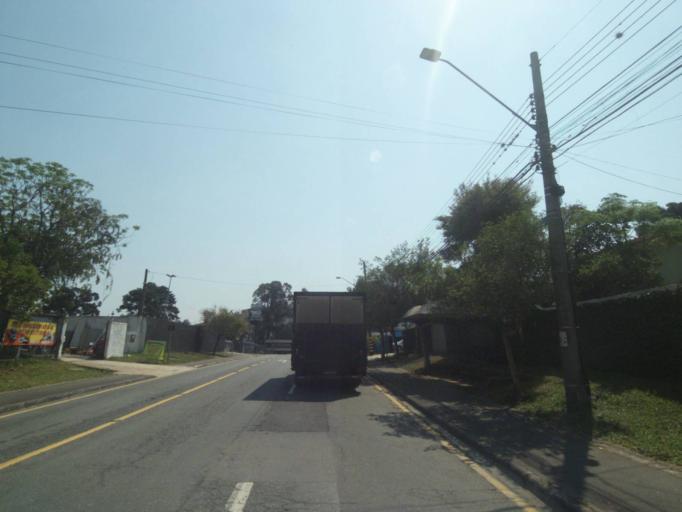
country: BR
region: Parana
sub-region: Curitiba
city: Curitiba
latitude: -25.4976
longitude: -49.2725
